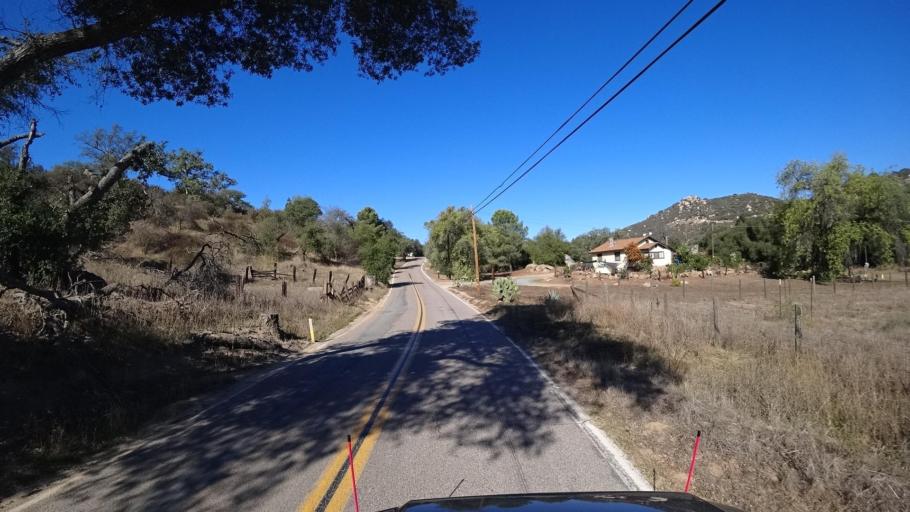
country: US
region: California
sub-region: San Diego County
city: Jamul
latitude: 32.7144
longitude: -116.7615
